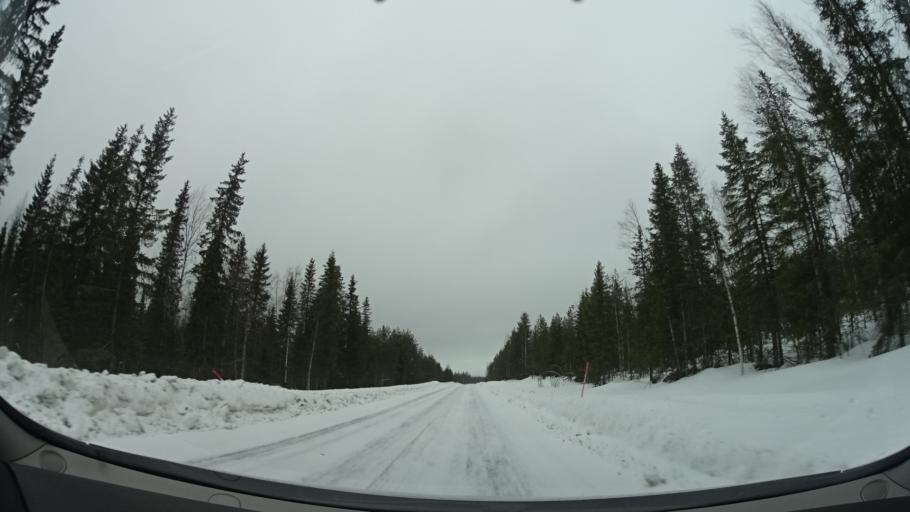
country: SE
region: Vaesterbotten
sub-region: Mala Kommun
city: Mala
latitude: 65.1031
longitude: 18.8967
